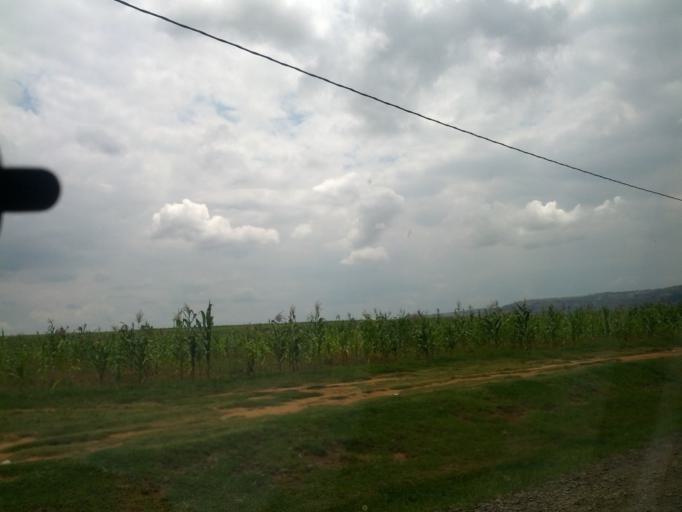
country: LS
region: Leribe
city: Leribe
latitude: -28.9321
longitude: 28.1534
